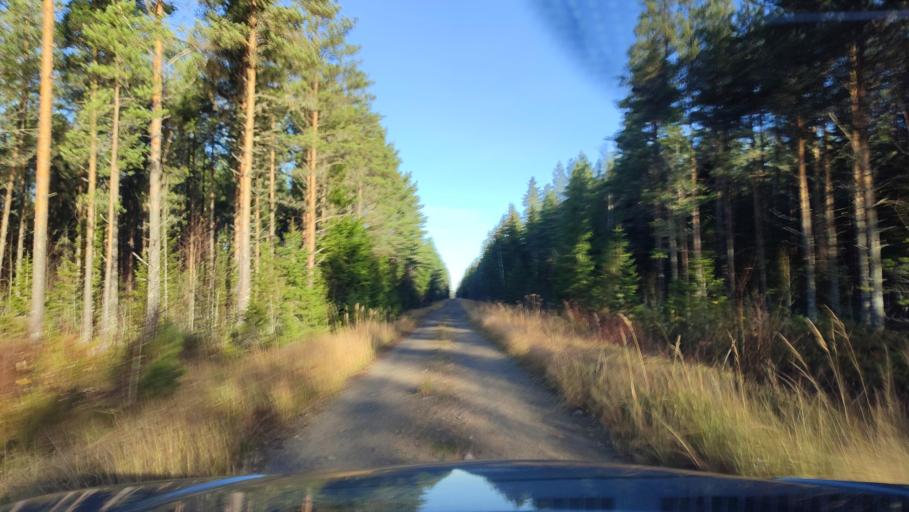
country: FI
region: Southern Ostrobothnia
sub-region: Suupohja
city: Karijoki
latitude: 62.1833
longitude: 21.6084
